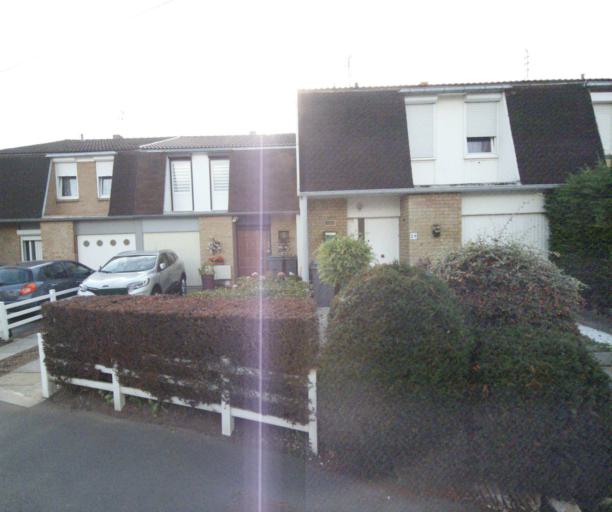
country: FR
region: Nord-Pas-de-Calais
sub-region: Departement du Nord
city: Santes
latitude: 50.5955
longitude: 2.9647
